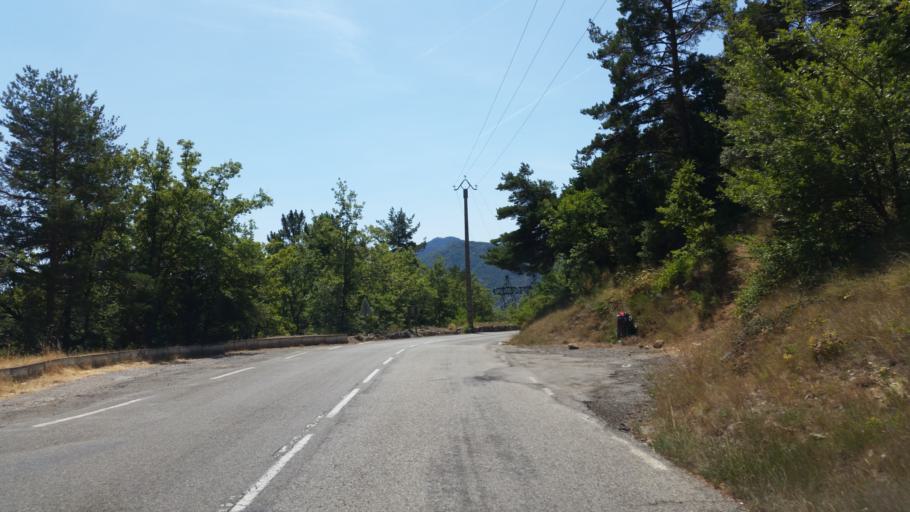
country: FR
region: Provence-Alpes-Cote d'Azur
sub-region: Departement des Alpes-Maritimes
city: Breil-sur-Roya
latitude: 43.9130
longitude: 7.4826
